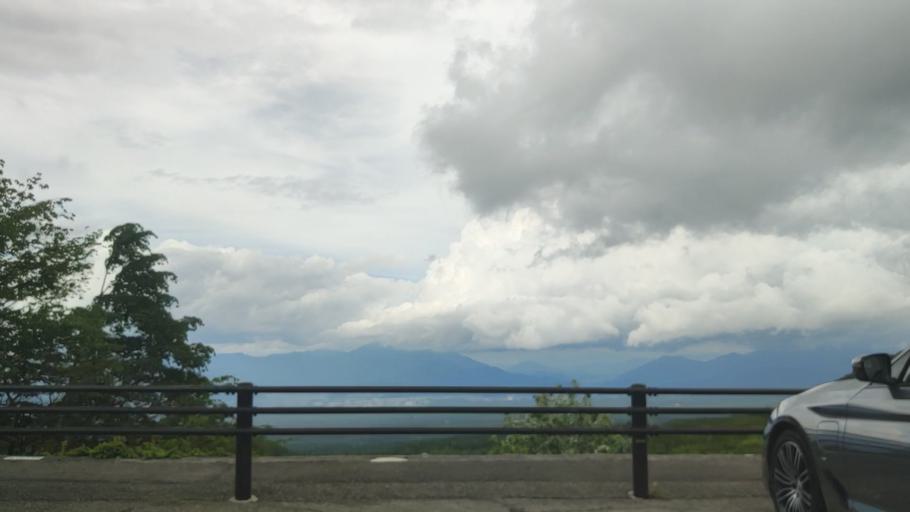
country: JP
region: Yamanashi
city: Fujikawaguchiko
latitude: 35.4156
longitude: 138.7018
